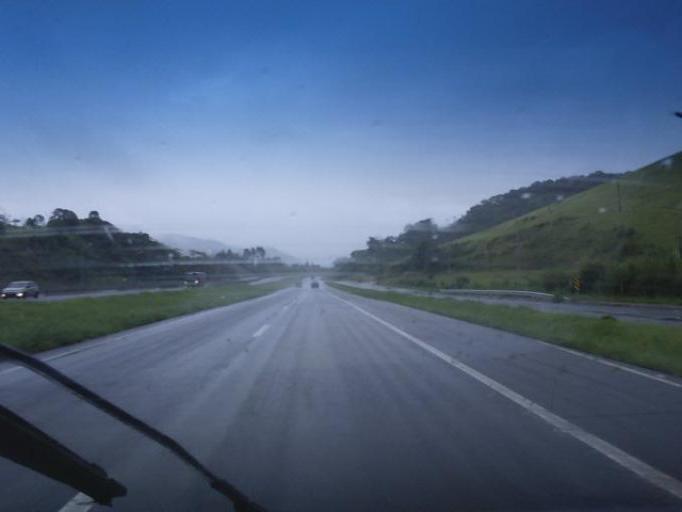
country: BR
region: Sao Paulo
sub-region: Juquia
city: Juquia
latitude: -24.3371
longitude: -47.6430
